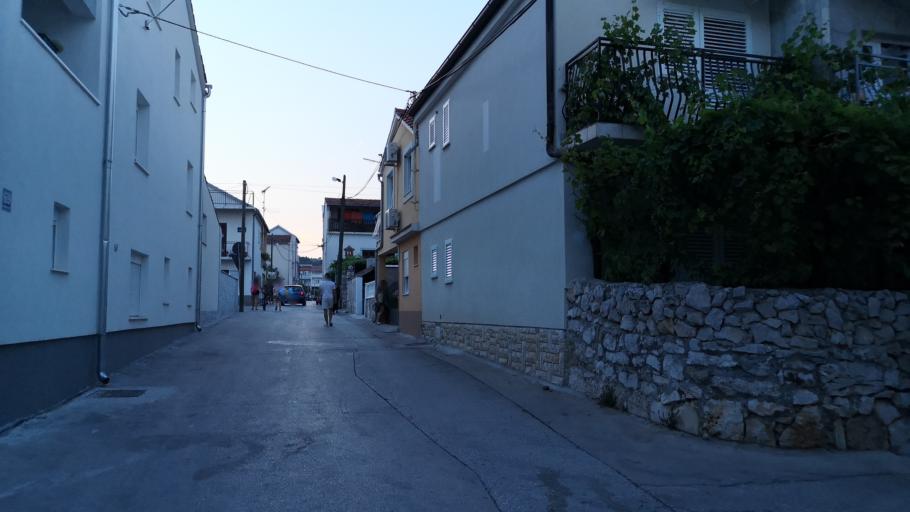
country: HR
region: Sibensko-Kniniska
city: Vodice
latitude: 43.7589
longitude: 15.7724
